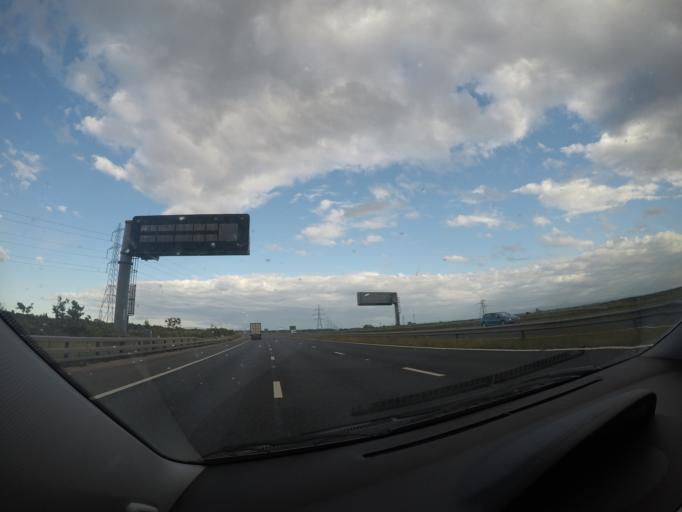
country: GB
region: Scotland
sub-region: Dumfries and Galloway
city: Gretna
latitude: 54.9864
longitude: -3.0364
